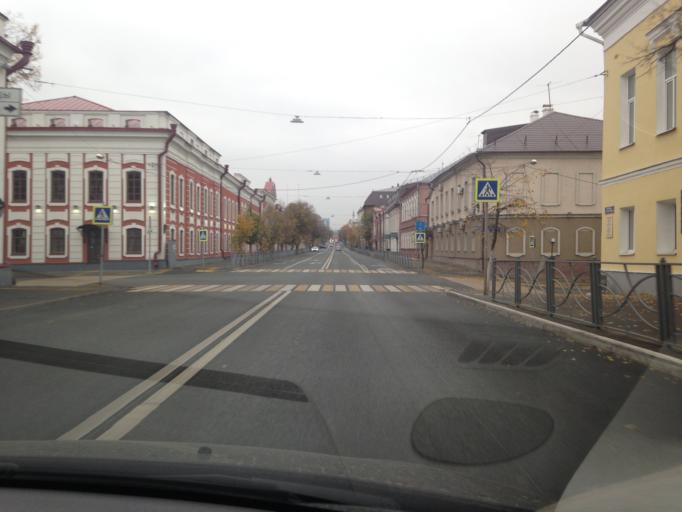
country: RU
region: Tatarstan
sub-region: Gorod Kazan'
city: Kazan
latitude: 55.7971
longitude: 49.1148
